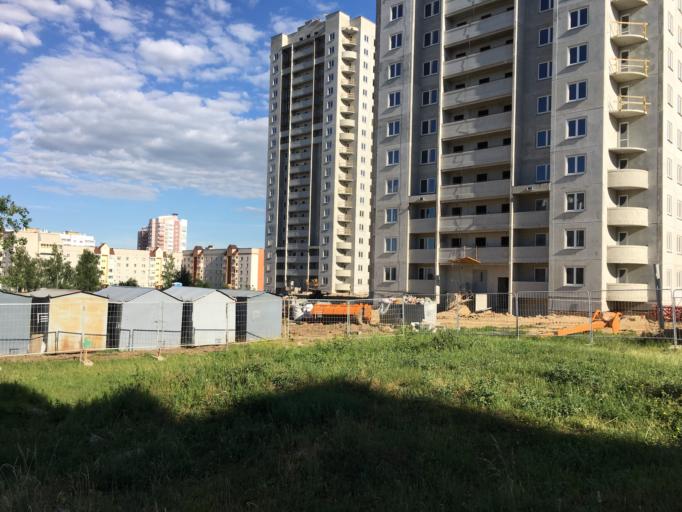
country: BY
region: Grodnenskaya
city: Hrodna
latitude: 53.7142
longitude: 23.8540
